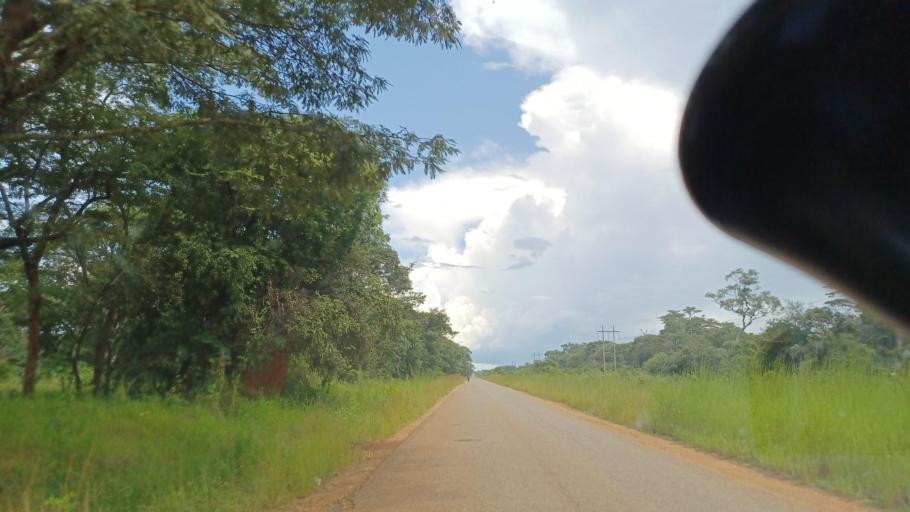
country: ZM
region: North-Western
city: Kasempa
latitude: -12.8784
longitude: 26.0445
